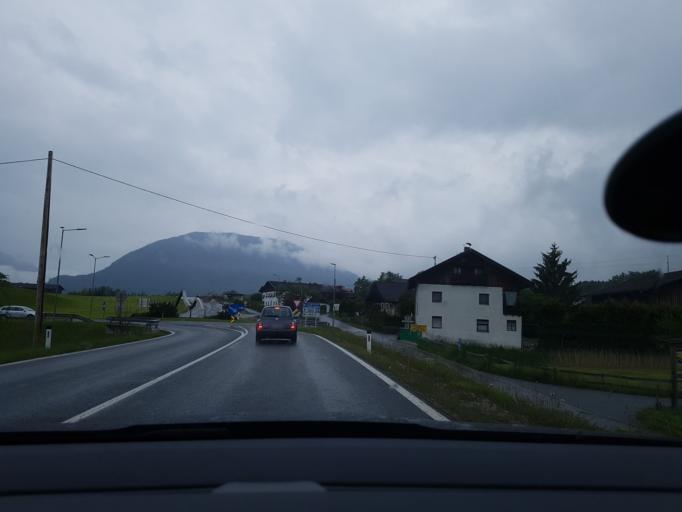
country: AT
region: Tyrol
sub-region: Politischer Bezirk Imst
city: Mieming
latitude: 47.3041
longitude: 10.9624
